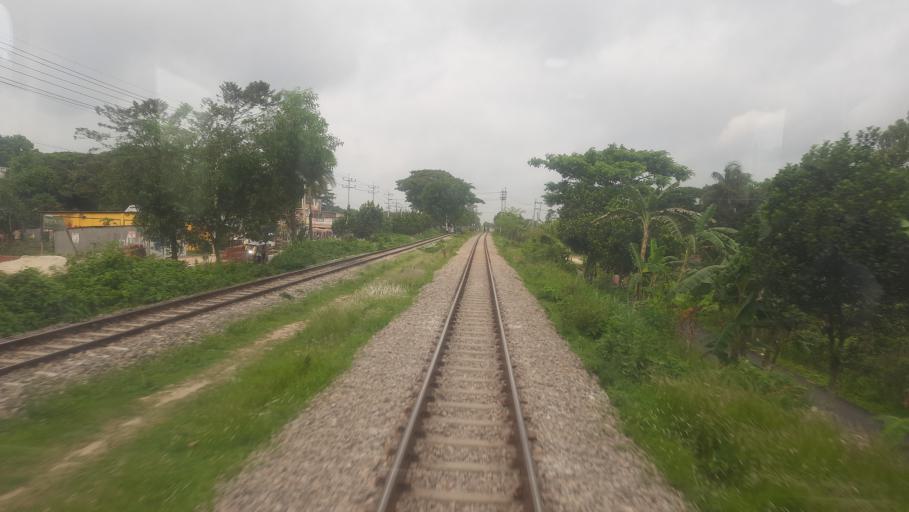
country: BD
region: Dhaka
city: Narsingdi
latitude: 23.9318
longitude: 90.7429
